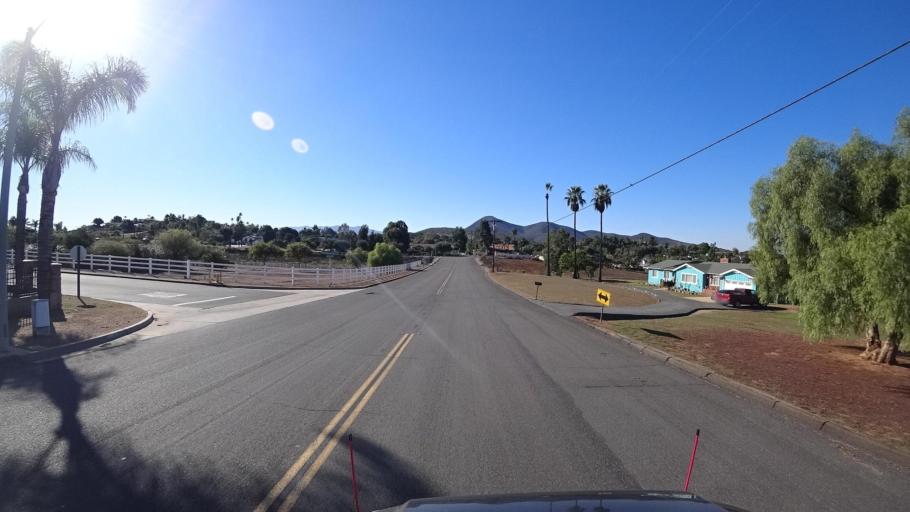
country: US
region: California
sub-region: San Diego County
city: Jamul
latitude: 32.7083
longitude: -116.8808
